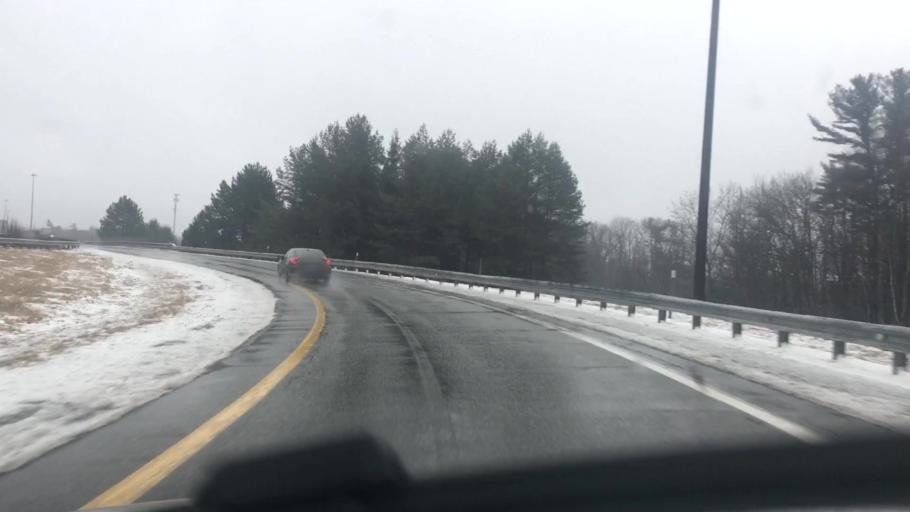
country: US
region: Maine
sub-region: York County
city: Saco
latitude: 43.5284
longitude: -70.4543
